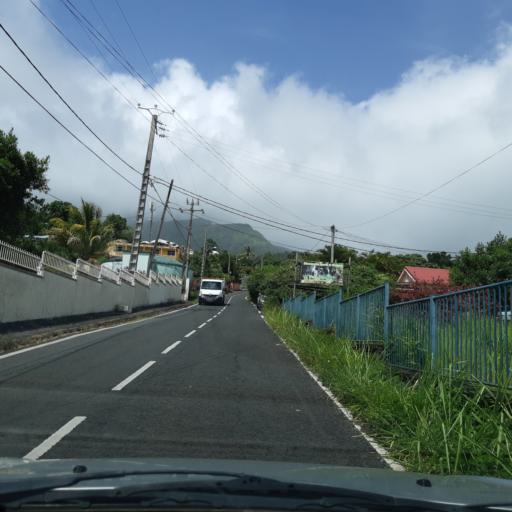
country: GP
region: Guadeloupe
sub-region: Guadeloupe
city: Saint-Claude
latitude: 16.0288
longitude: -61.6921
